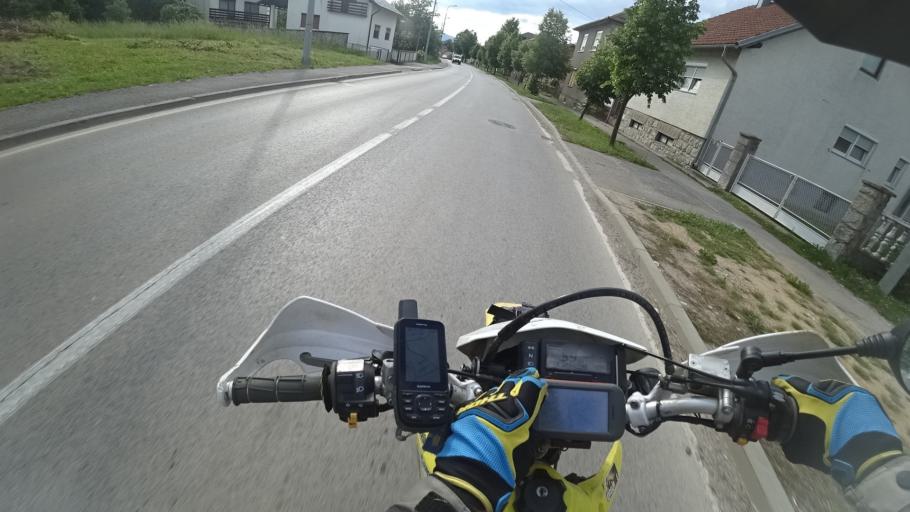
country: HR
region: Licko-Senjska
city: Gospic
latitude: 44.5401
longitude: 15.3823
